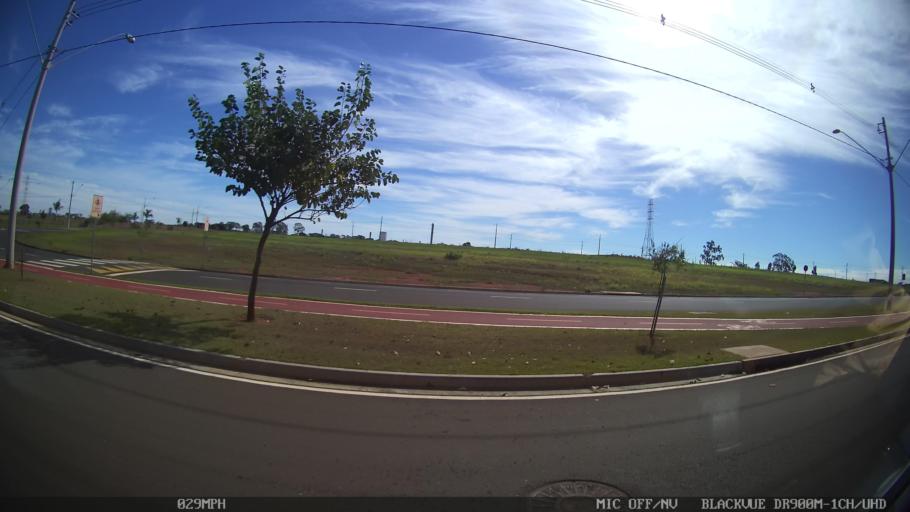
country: BR
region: Sao Paulo
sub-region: Sao Jose Do Rio Preto
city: Sao Jose do Rio Preto
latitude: -20.8530
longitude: -49.3747
